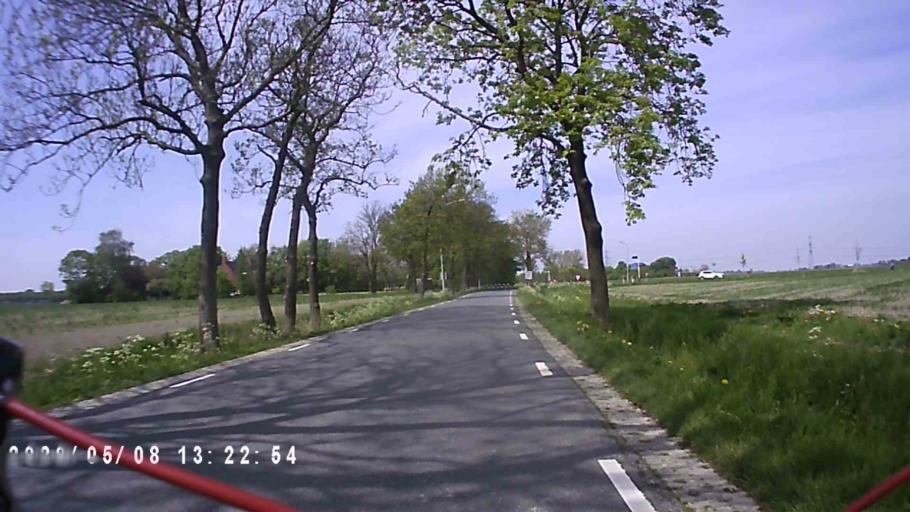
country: NL
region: Groningen
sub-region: Gemeente Bedum
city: Bedum
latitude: 53.3268
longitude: 6.7105
